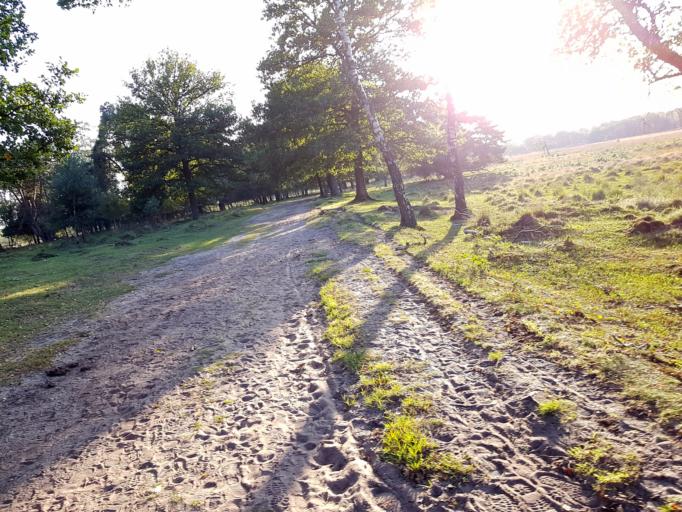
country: NL
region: Utrecht
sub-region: Gemeente Utrechtse Heuvelrug
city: Leersum
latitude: 52.0402
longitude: 5.4402
